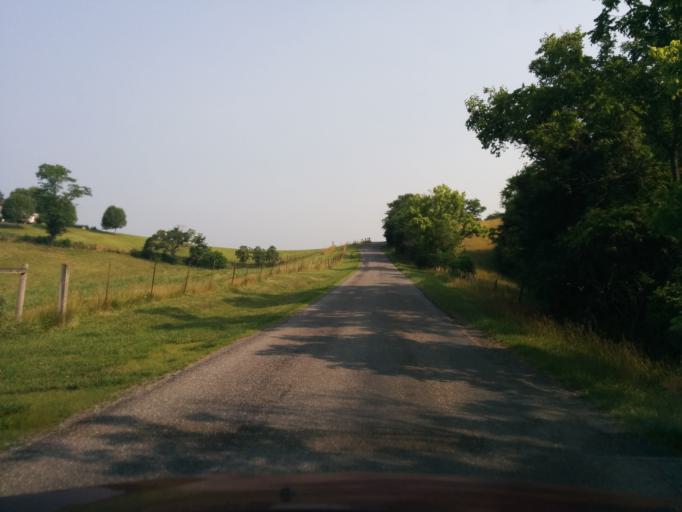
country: US
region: Virginia
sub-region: City of Lexington
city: Lexington
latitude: 37.7567
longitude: -79.4398
